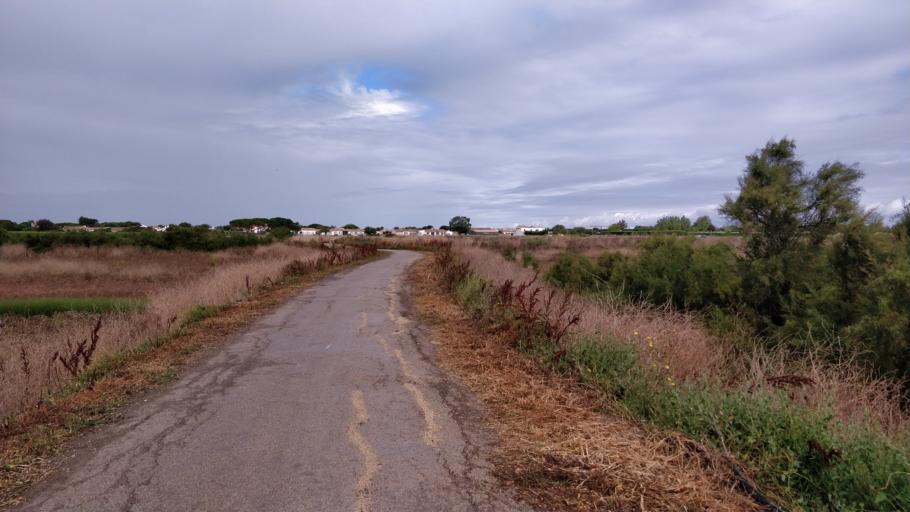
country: FR
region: Poitou-Charentes
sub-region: Departement de la Charente-Maritime
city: La Couarde-sur-Mer
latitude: 46.2233
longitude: -1.4241
